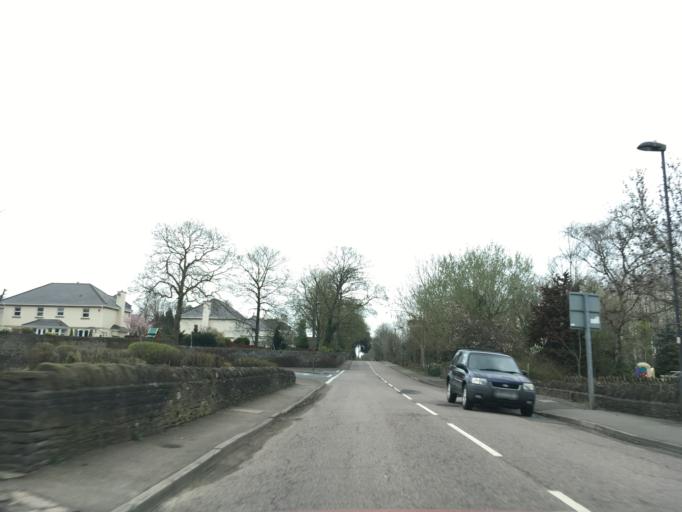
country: GB
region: England
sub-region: South Gloucestershire
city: Winterbourne
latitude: 51.5208
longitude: -2.4998
